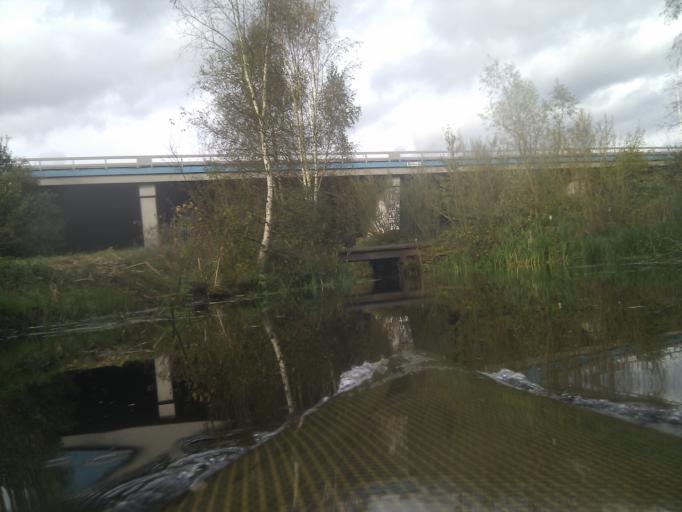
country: NL
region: Utrecht
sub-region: Gemeente Bunnik
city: Bunnik
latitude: 52.0925
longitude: 5.2007
